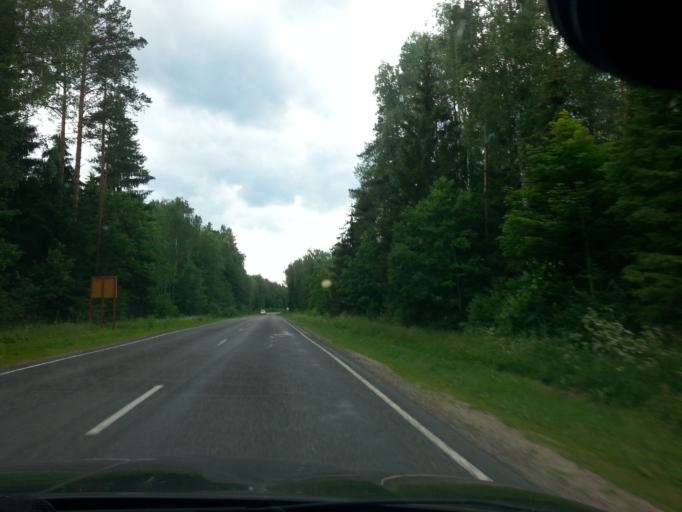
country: BY
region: Minsk
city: Svir
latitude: 54.8518
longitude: 26.2701
